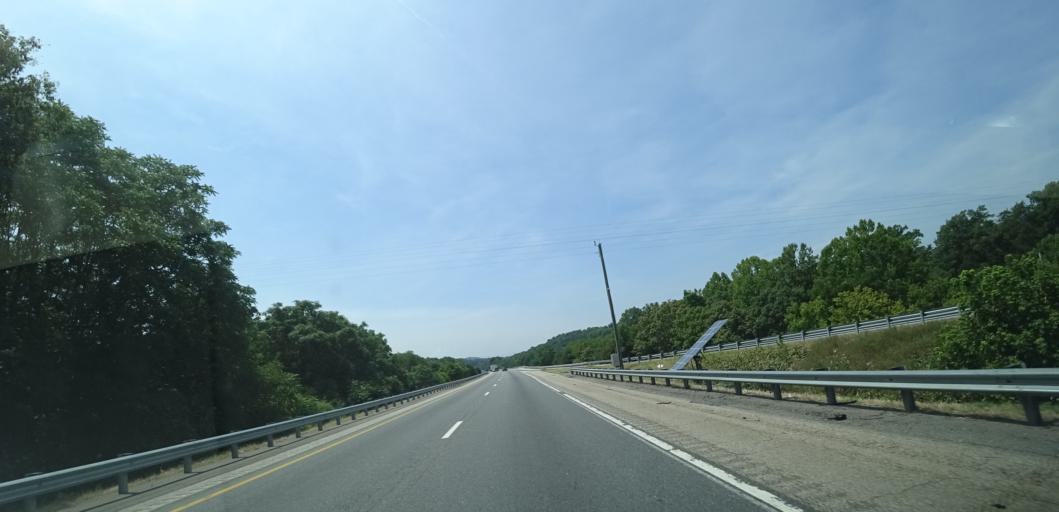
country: US
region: Virginia
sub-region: Rockbridge County
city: East Lexington
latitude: 37.7914
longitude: -79.3989
